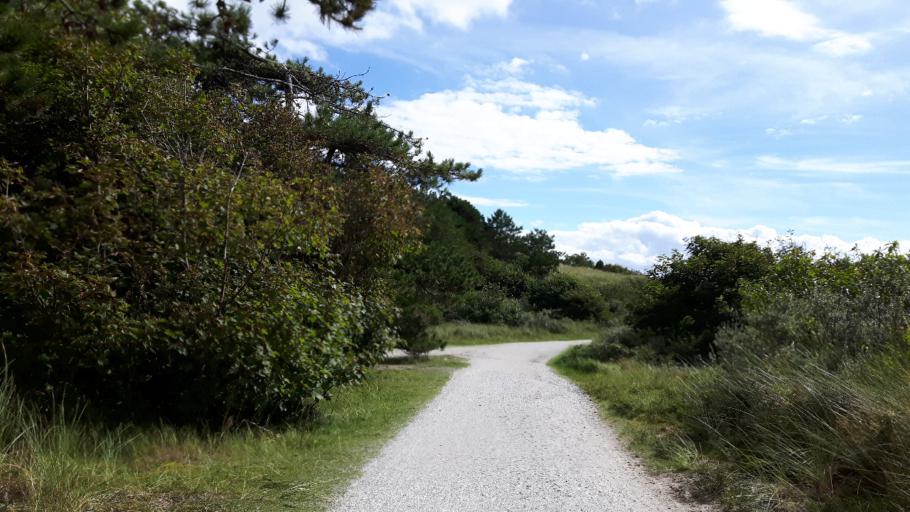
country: NL
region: Friesland
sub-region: Gemeente Ameland
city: Hollum
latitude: 53.4425
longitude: 5.6186
